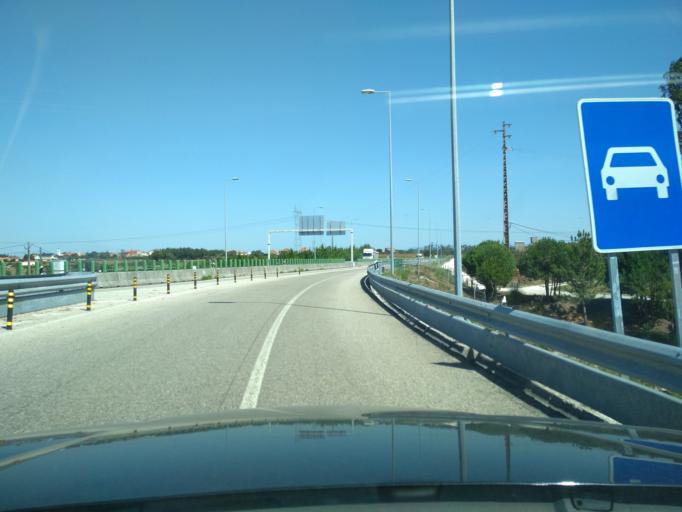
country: PT
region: Leiria
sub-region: Pombal
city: Lourical
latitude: 39.9881
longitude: -8.7865
